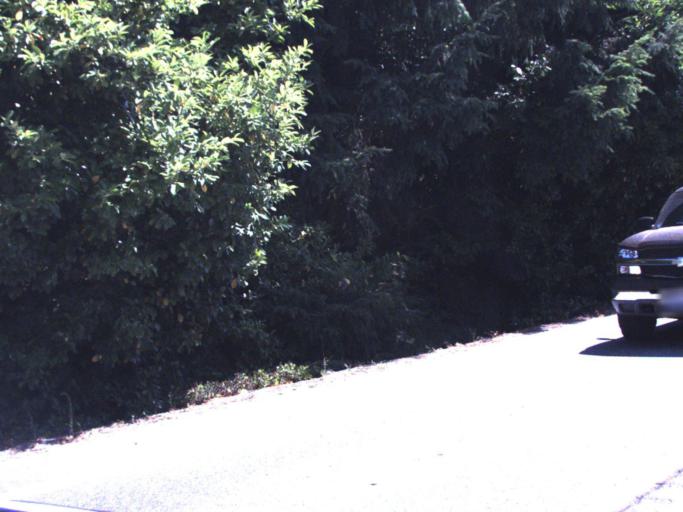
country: US
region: Washington
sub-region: King County
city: Union Hill-Novelty Hill
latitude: 47.6488
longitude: -122.0434
